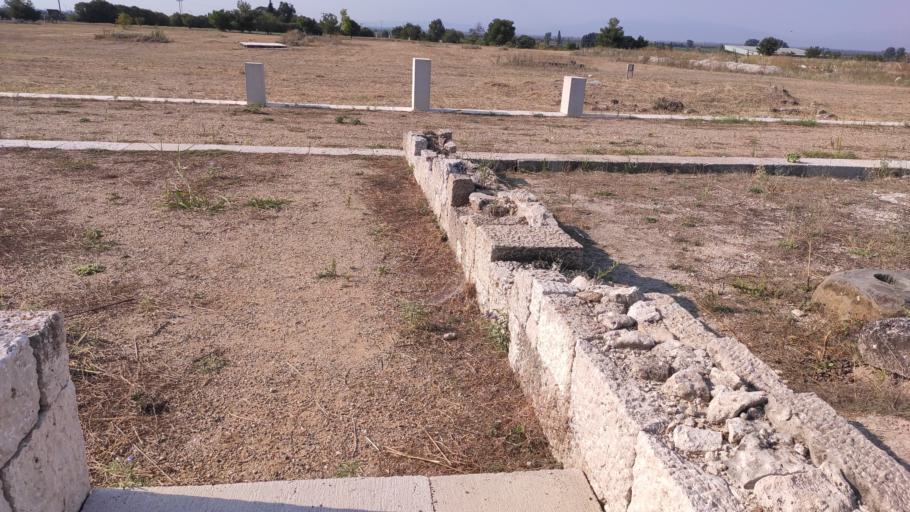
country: GR
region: Central Macedonia
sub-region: Nomos Pellis
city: Pella
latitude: 40.7570
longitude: 22.5193
